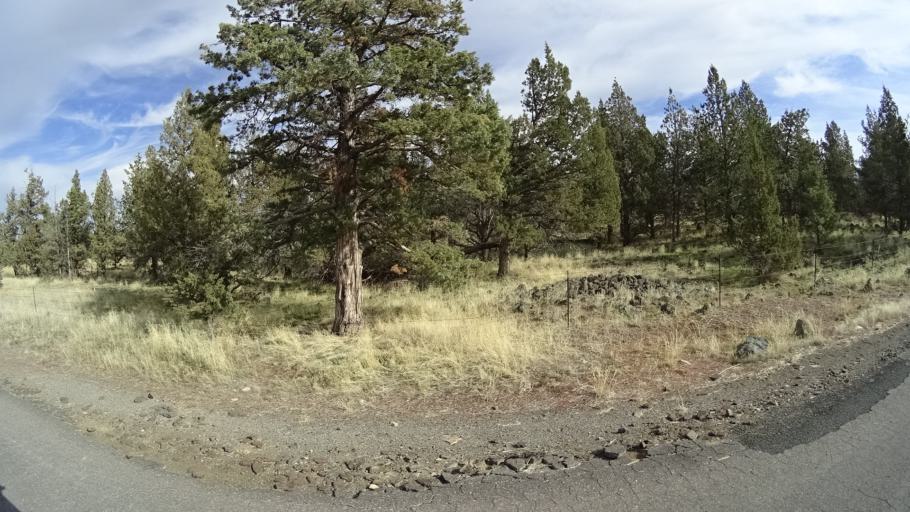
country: US
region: California
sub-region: Siskiyou County
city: Montague
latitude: 41.6021
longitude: -122.4040
